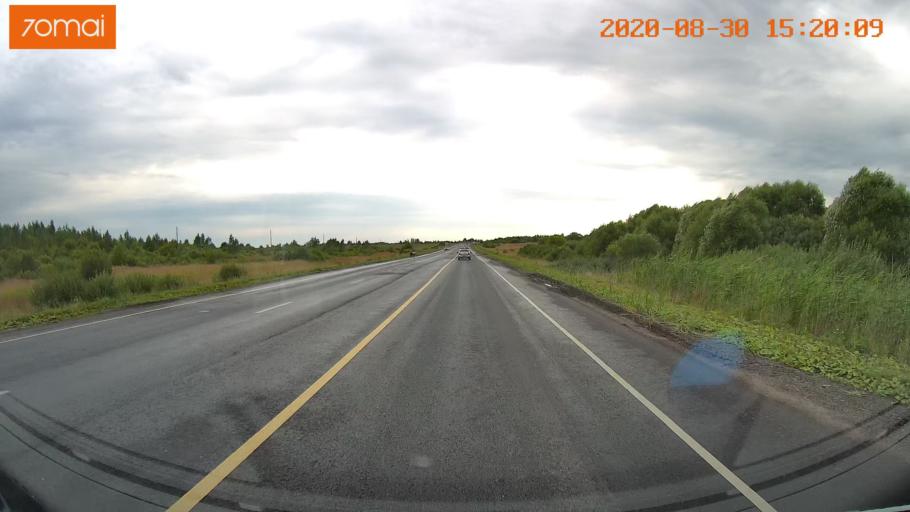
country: RU
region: Ivanovo
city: Rodniki
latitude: 57.1035
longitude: 41.7738
